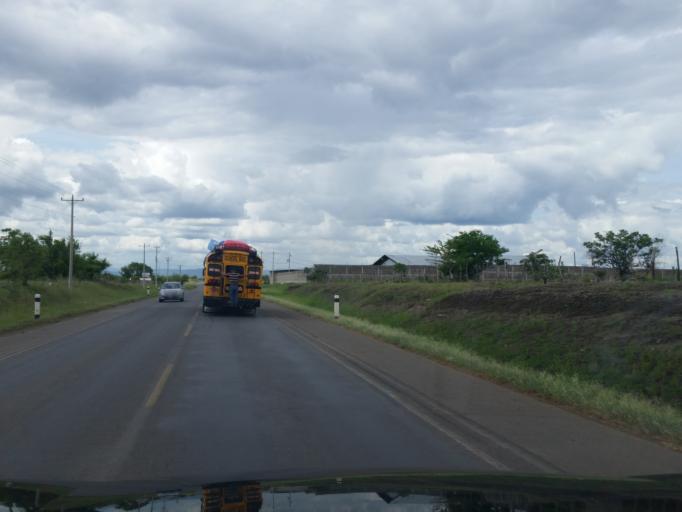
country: NI
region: Managua
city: Tipitapa
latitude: 12.2408
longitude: -86.0909
